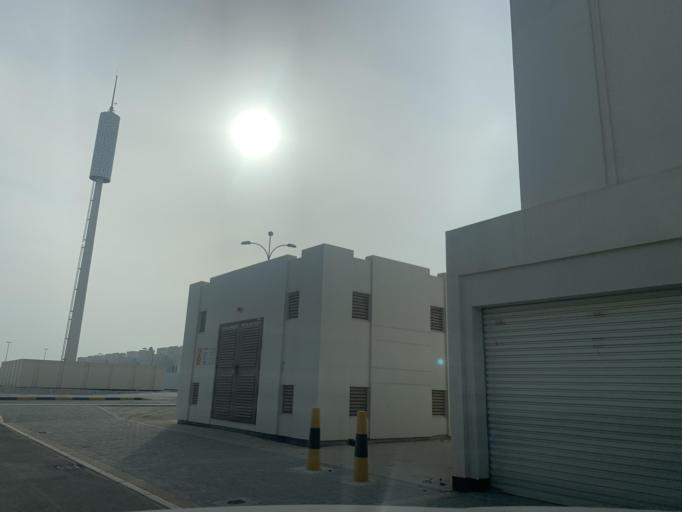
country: BH
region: Muharraq
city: Al Muharraq
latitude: 26.3167
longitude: 50.6288
